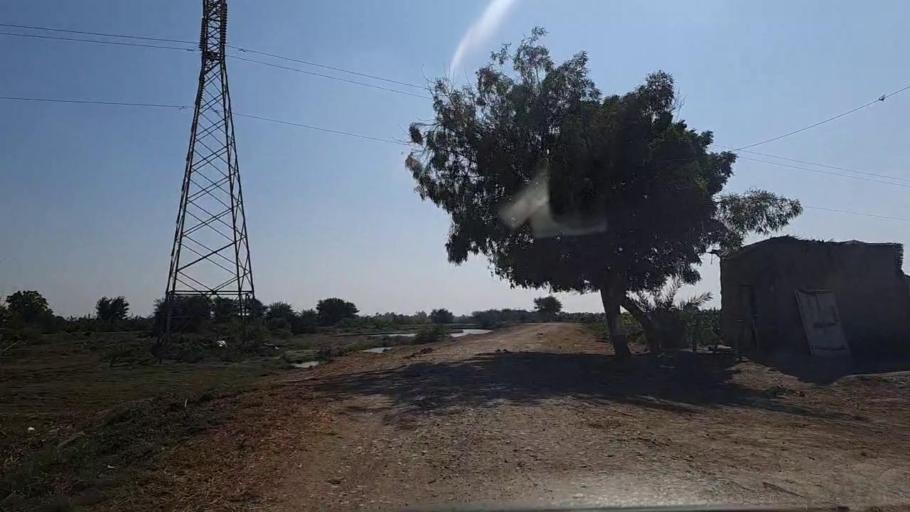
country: PK
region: Sindh
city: Mirpur Batoro
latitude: 24.6869
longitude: 68.1853
